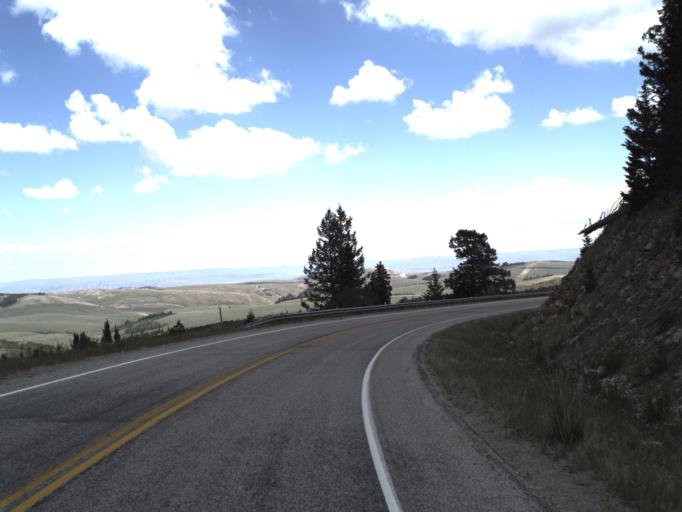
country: US
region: Utah
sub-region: Rich County
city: Randolph
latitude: 41.4761
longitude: -111.4632
